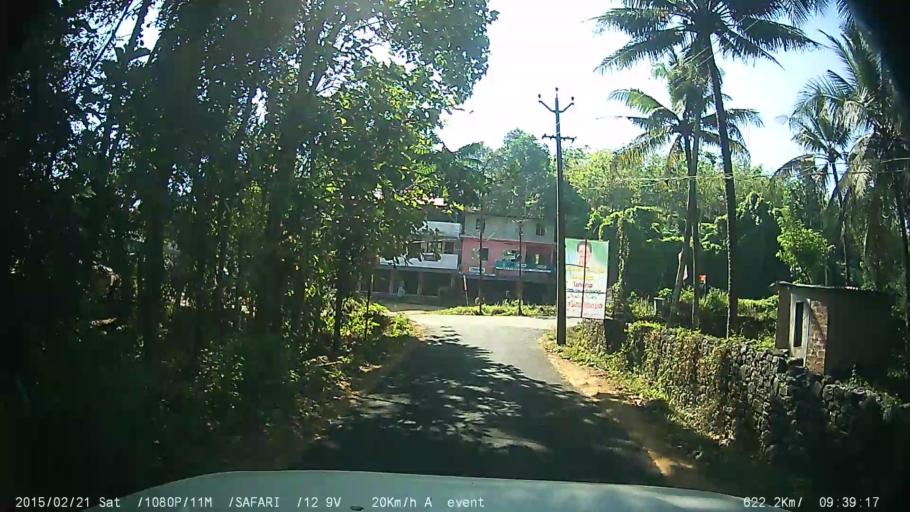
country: IN
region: Kerala
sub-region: Kottayam
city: Palackattumala
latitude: 9.7839
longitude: 76.5747
